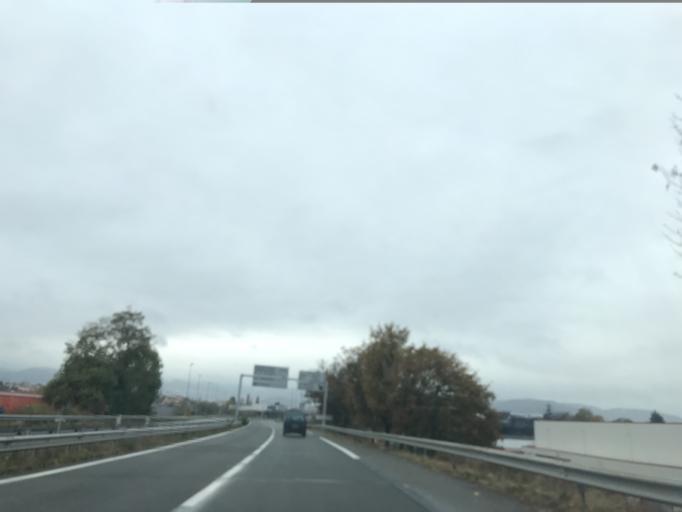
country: FR
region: Auvergne
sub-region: Departement du Puy-de-Dome
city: Aubiere
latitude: 45.7758
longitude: 3.1365
